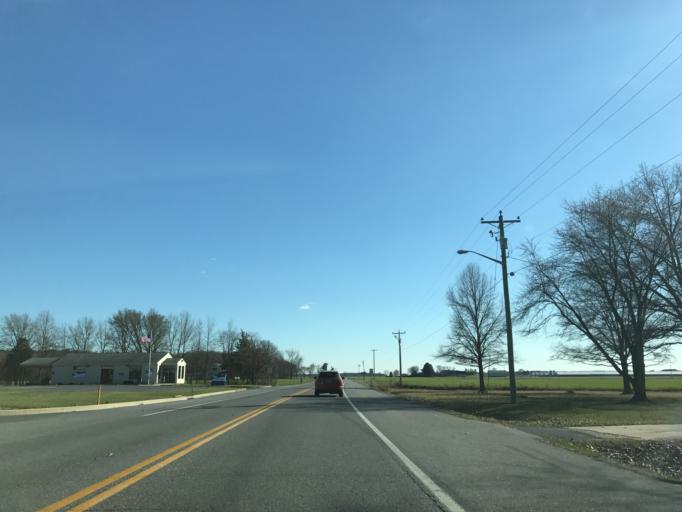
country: US
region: Maryland
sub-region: Caroline County
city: Greensboro
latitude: 39.1408
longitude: -75.8639
